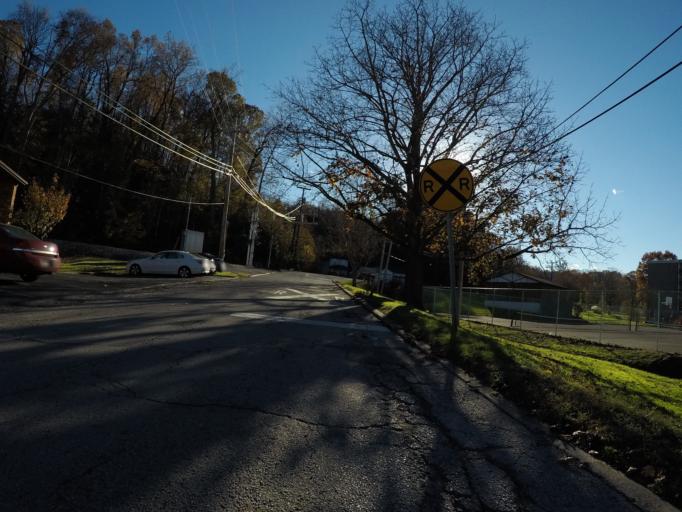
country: US
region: West Virginia
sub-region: Wayne County
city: Ceredo
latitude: 38.3917
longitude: -82.5618
